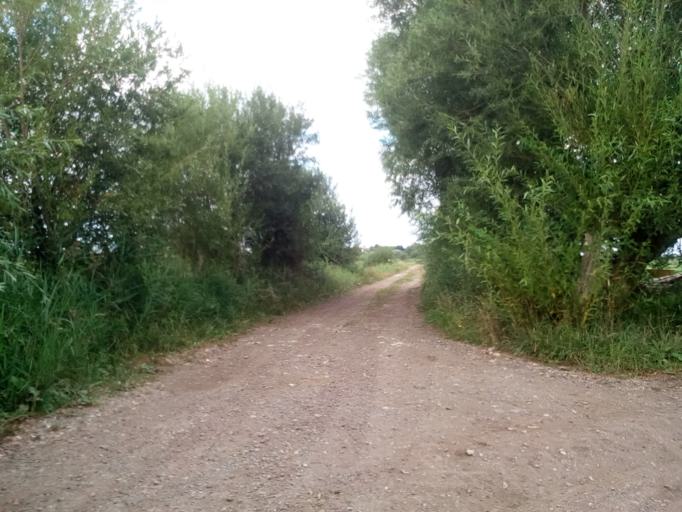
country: FR
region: Lower Normandy
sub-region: Departement du Calvados
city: Troarn
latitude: 49.1746
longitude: -0.1647
